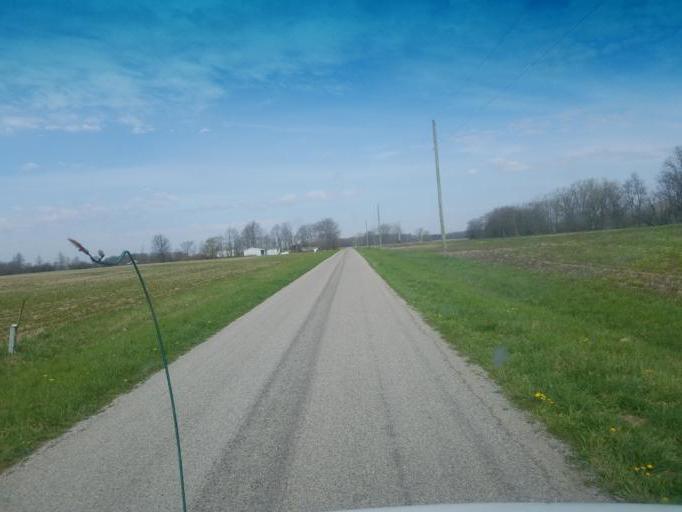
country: US
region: Ohio
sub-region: Union County
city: Richwood
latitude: 40.4832
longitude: -83.4444
